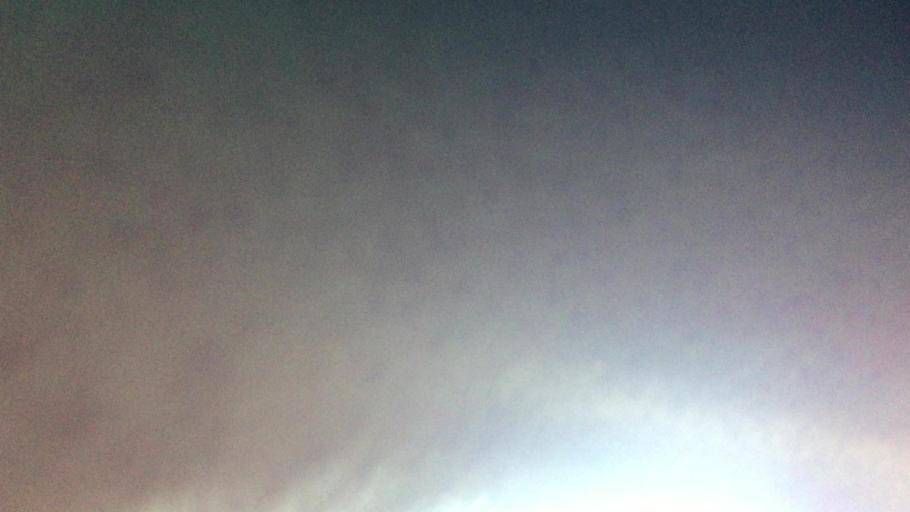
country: US
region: Georgia
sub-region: Carroll County
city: Carrollton
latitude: 33.5954
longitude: -85.0380
